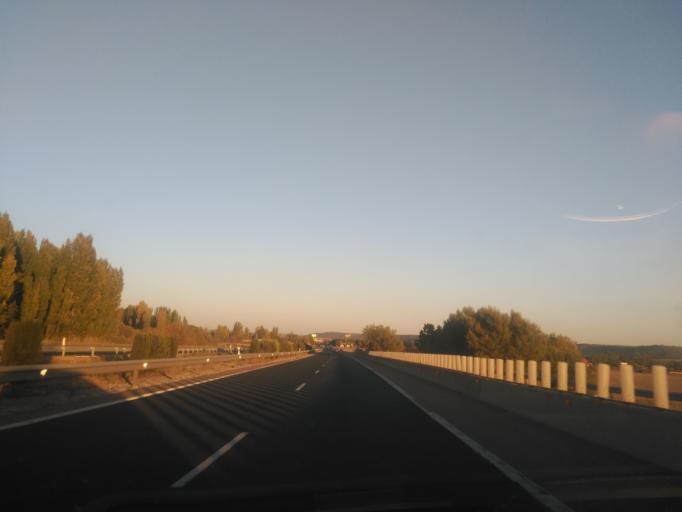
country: ES
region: Castille and Leon
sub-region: Provincia de Valladolid
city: Tudela de Duero
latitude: 41.5935
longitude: -4.6174
